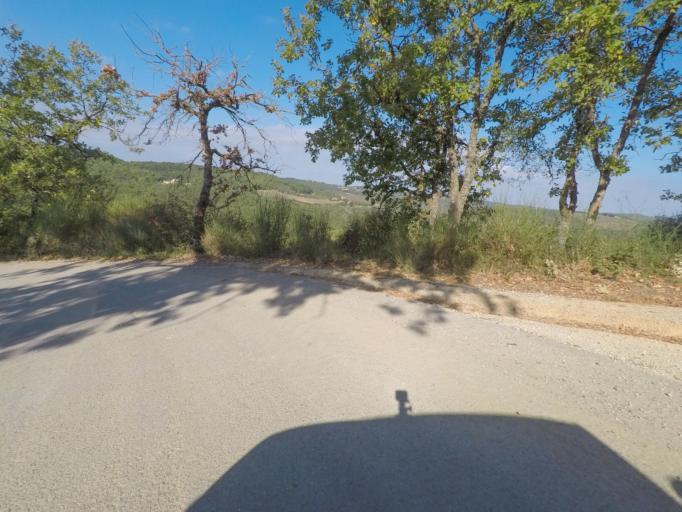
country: IT
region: Tuscany
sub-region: Provincia di Siena
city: Castellina in Chianti
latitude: 43.4375
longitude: 11.3254
